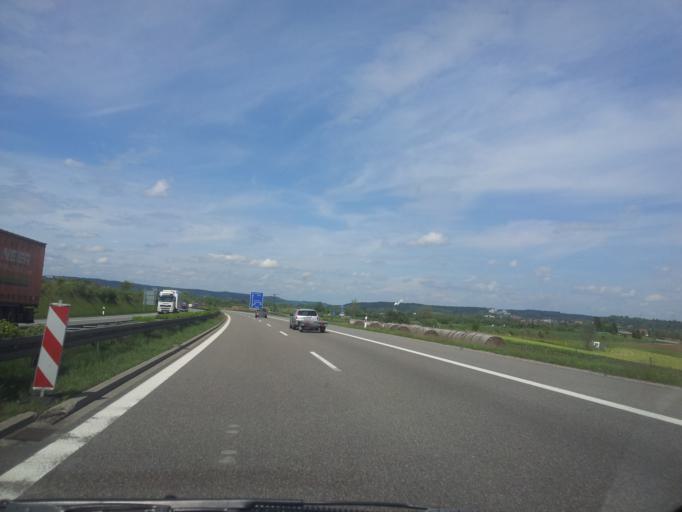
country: DE
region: Baden-Wuerttemberg
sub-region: Tuebingen Region
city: Leutkirch im Allgau
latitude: 47.8072
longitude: 9.9888
